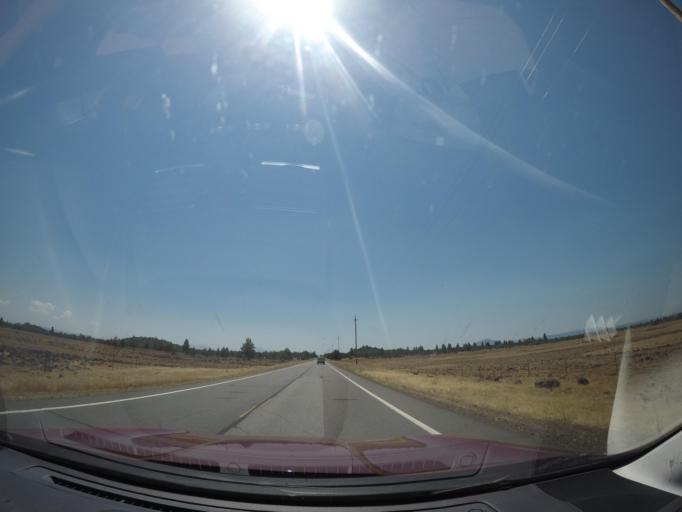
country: US
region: California
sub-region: Shasta County
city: Burney
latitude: 41.0975
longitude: -121.2983
